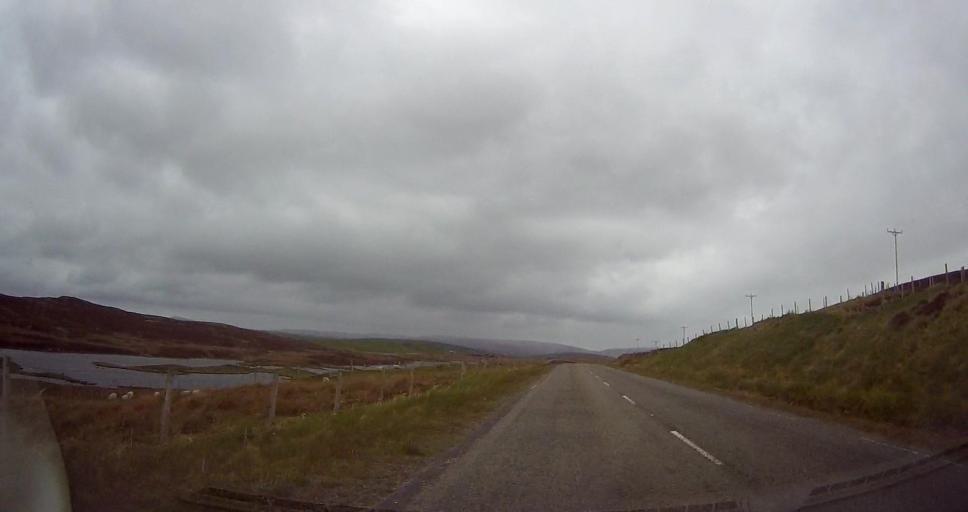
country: GB
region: Scotland
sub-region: Shetland Islands
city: Sandwick
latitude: 60.2583
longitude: -1.4787
